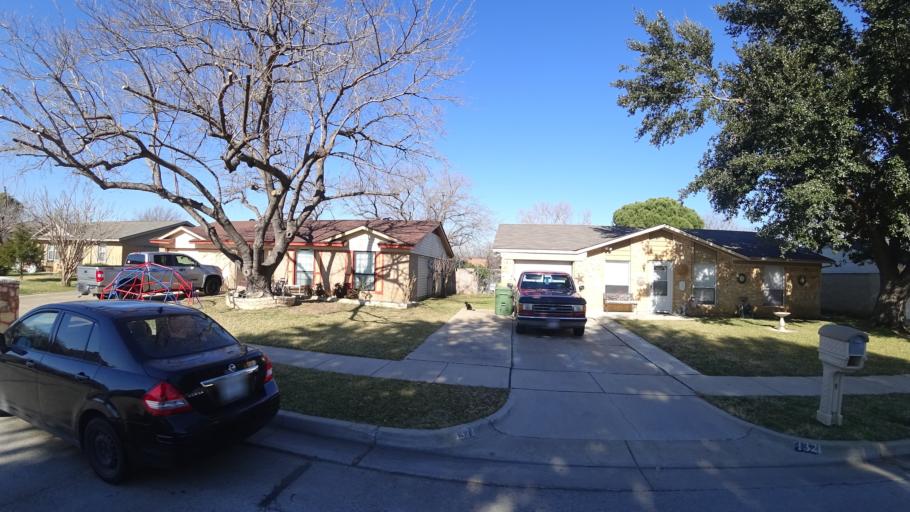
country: US
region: Texas
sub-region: Denton County
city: Lewisville
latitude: 33.0315
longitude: -97.0144
